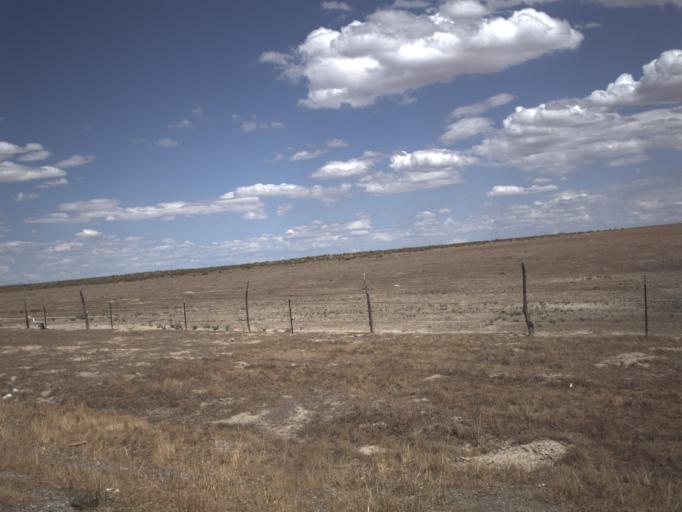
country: US
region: Utah
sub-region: Millard County
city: Delta
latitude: 39.3318
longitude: -112.4877
